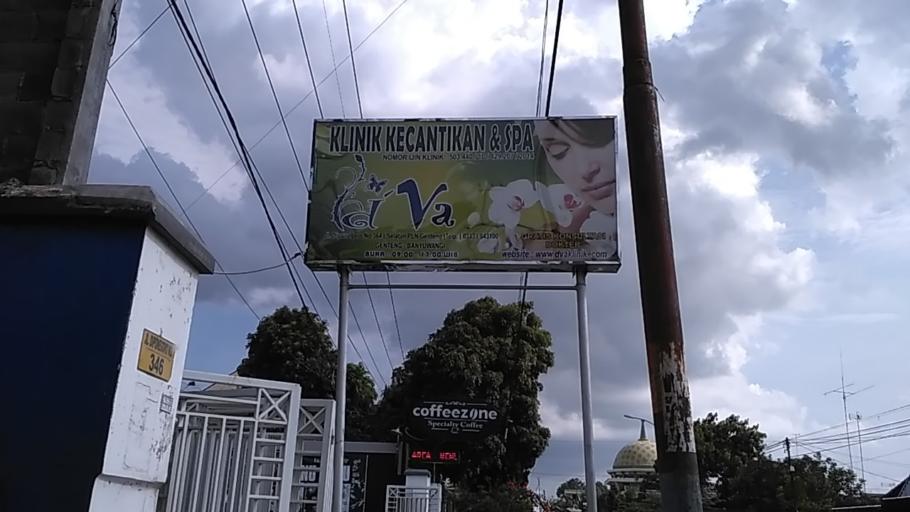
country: ID
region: East Java
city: Genteng
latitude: -8.3718
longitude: 114.1457
